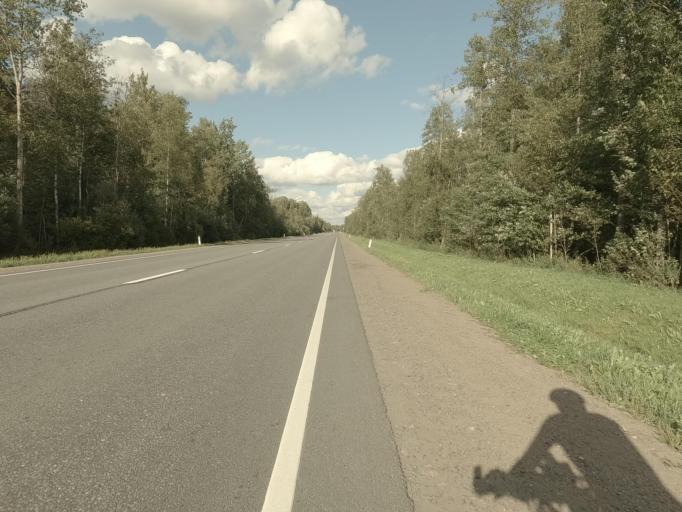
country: RU
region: Leningrad
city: Nikol'skoye
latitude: 59.6557
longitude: 30.8618
